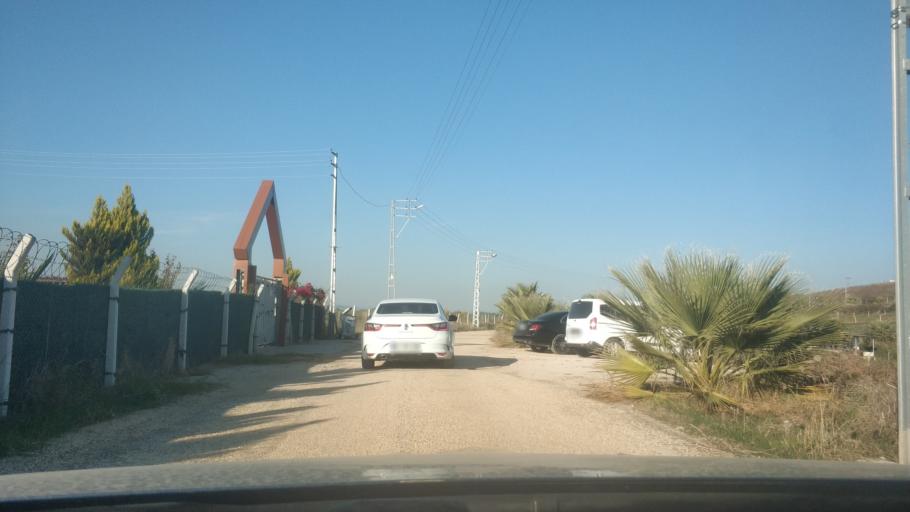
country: TR
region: Adana
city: Adana
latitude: 37.0912
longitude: 35.3034
